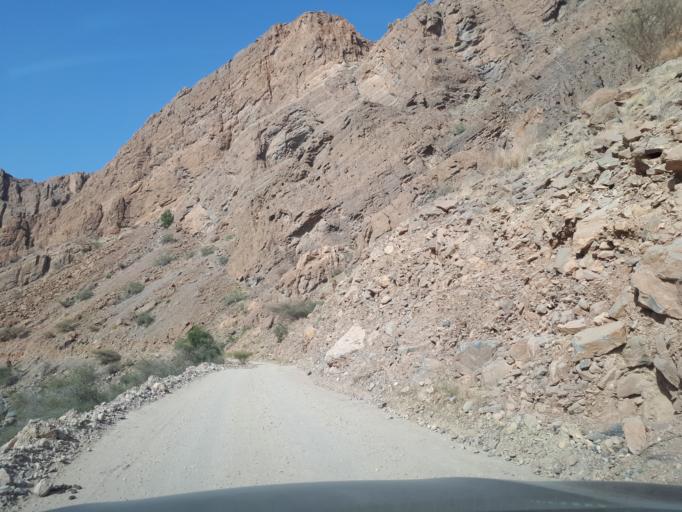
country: OM
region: Ash Sharqiyah
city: Al Qabil
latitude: 23.0599
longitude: 58.9865
